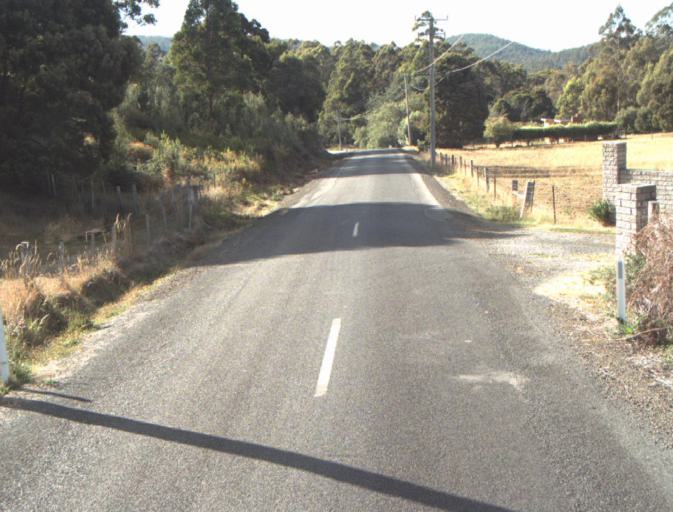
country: AU
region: Tasmania
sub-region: Launceston
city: Mayfield
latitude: -41.2829
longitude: 147.1966
